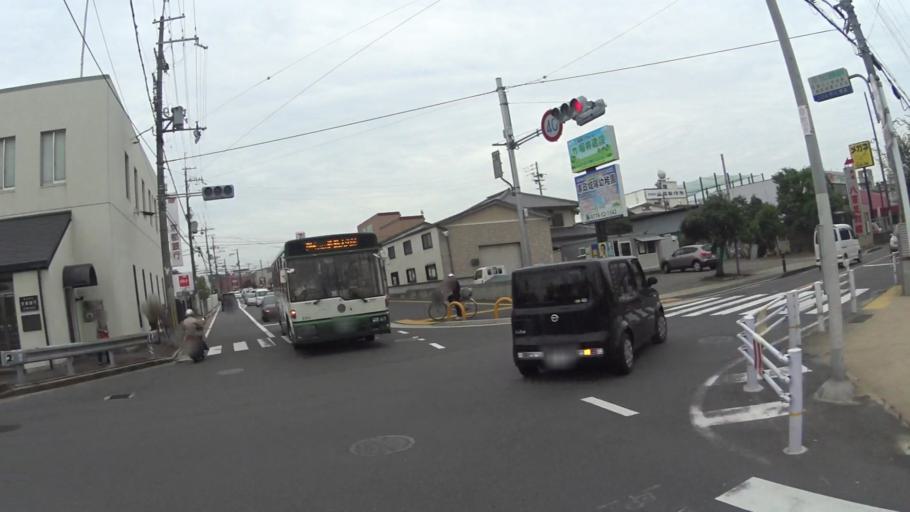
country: JP
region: Kyoto
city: Uji
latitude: 34.8643
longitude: 135.7768
